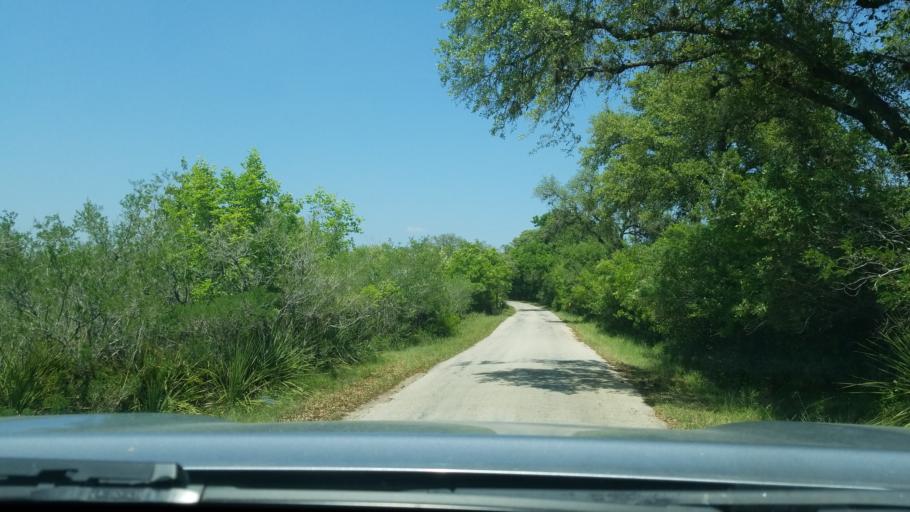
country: US
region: Texas
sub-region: Blanco County
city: Blanco
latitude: 30.0104
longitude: -98.4366
